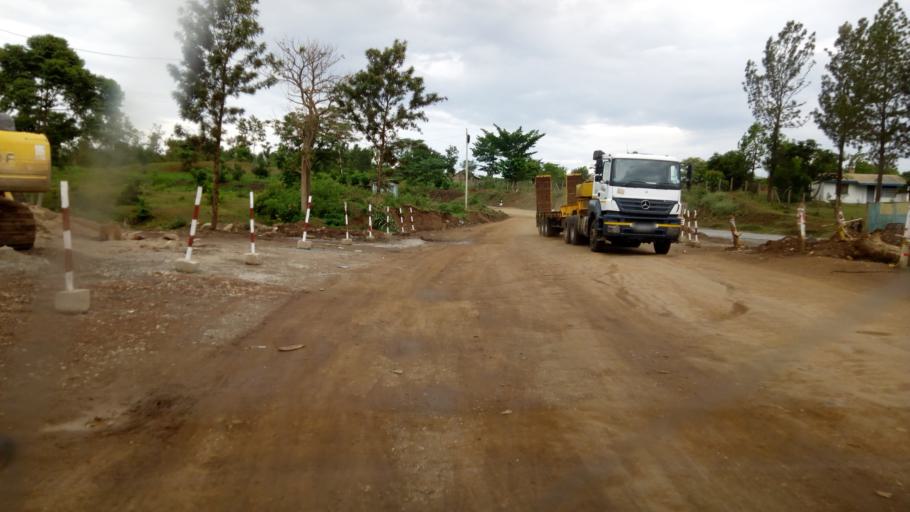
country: UG
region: Eastern Region
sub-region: Mbale District
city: Mbale
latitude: 0.9368
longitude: 34.1579
